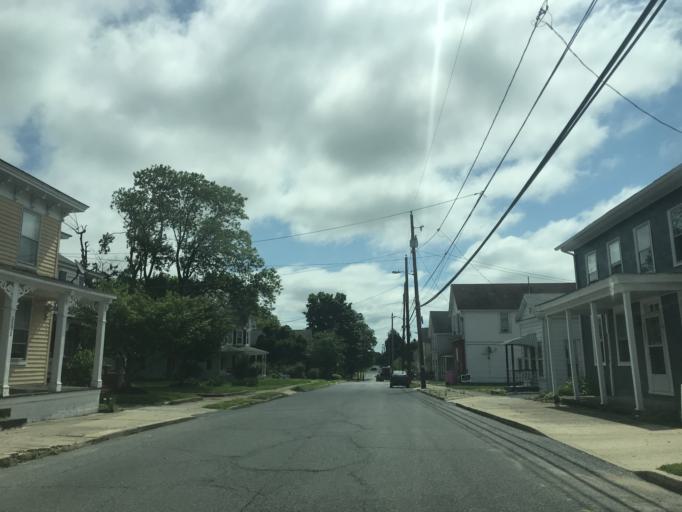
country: US
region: Maryland
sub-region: Caroline County
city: Ridgely
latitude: 38.9170
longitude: -75.9416
